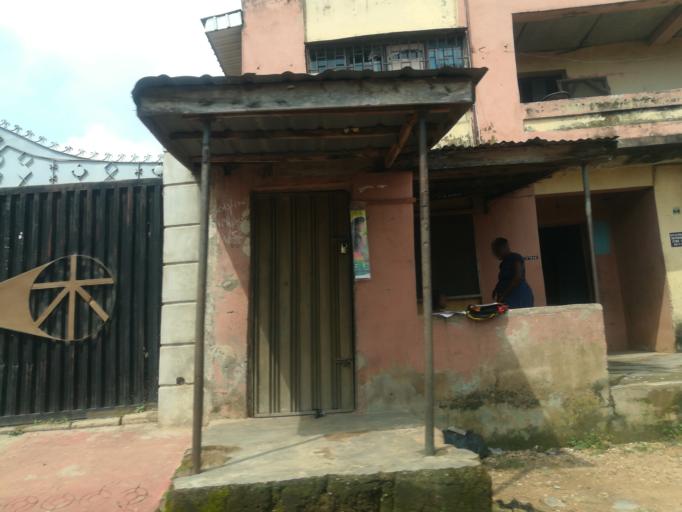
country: NG
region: Oyo
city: Ibadan
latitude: 7.4154
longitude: 3.9532
